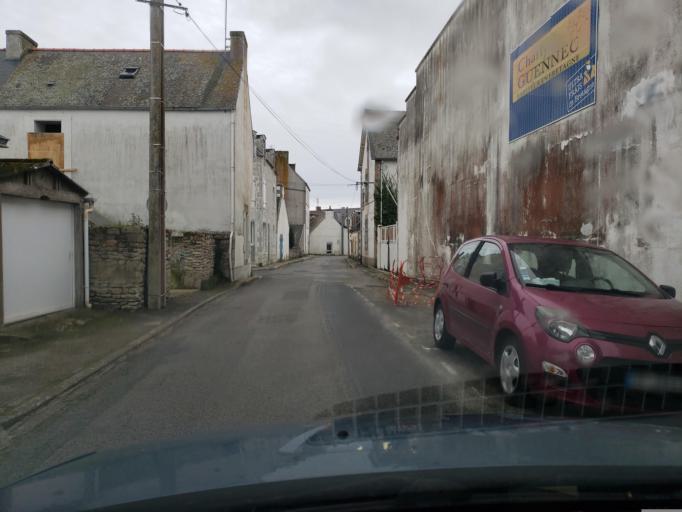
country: FR
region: Brittany
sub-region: Departement du Finistere
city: Guilvinec
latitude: 47.7983
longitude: -4.2829
